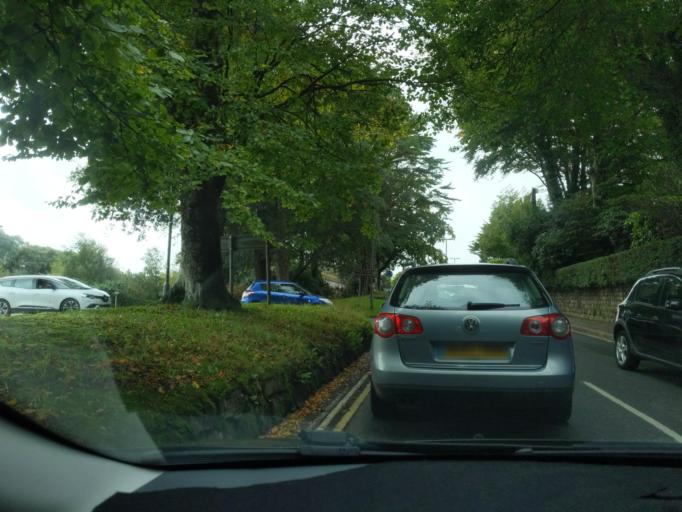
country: GB
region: England
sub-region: Cornwall
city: St Austell
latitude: 50.3400
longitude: -4.7835
